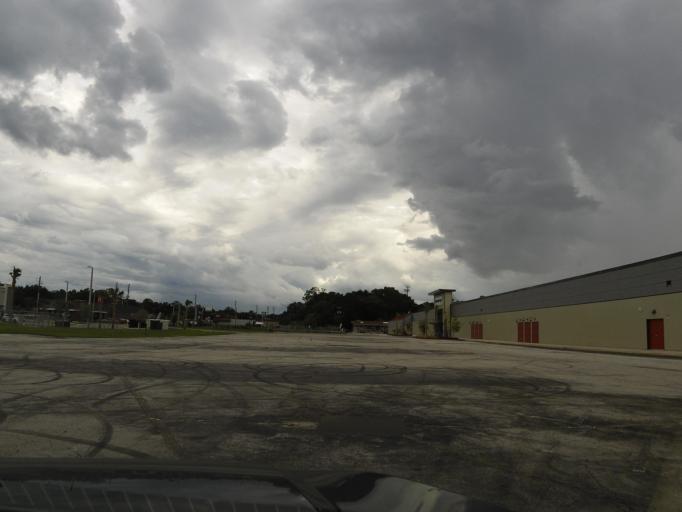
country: US
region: Florida
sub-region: Duval County
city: Jacksonville
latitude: 30.2944
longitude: -81.6035
